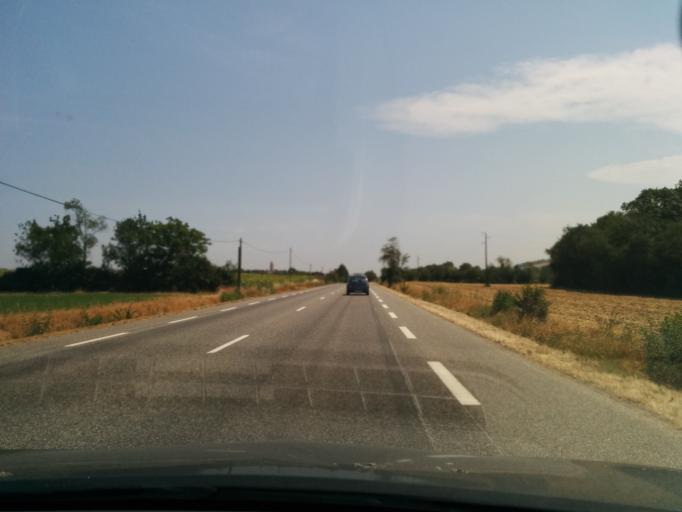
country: FR
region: Midi-Pyrenees
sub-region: Departement de la Haute-Garonne
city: Avignonet-Lauragais
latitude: 43.3734
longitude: 1.7636
